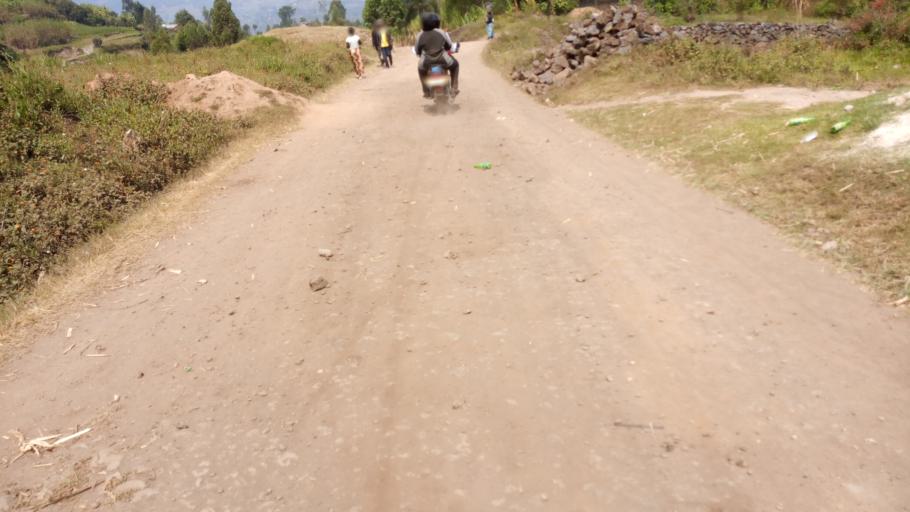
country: UG
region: Western Region
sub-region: Kisoro District
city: Kisoro
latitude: -1.3314
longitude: 29.7602
